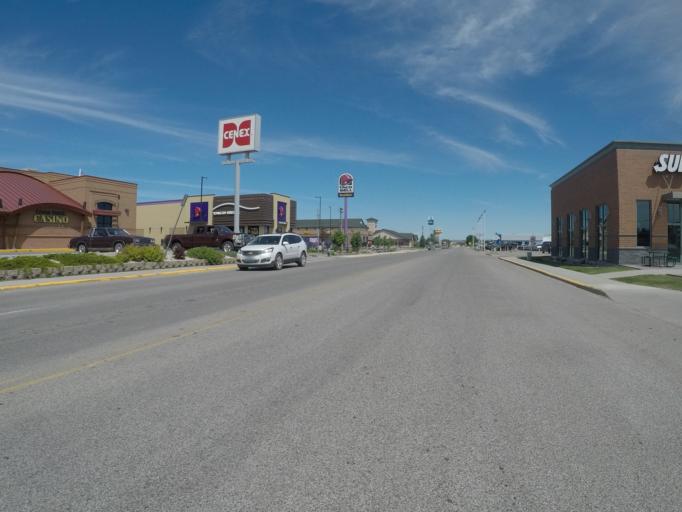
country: US
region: Montana
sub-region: Yellowstone County
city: Laurel
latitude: 45.6653
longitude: -108.7711
